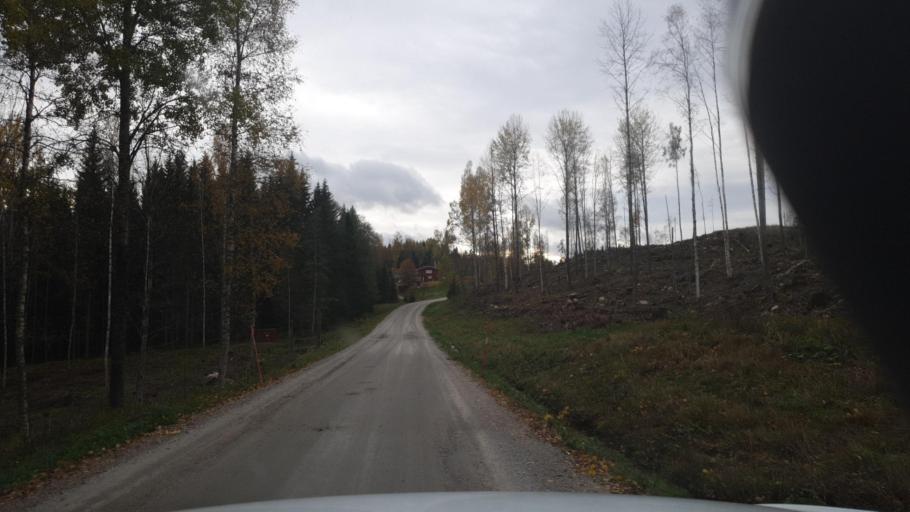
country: SE
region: Vaermland
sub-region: Arvika Kommun
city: Arvika
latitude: 59.8283
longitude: 12.7470
